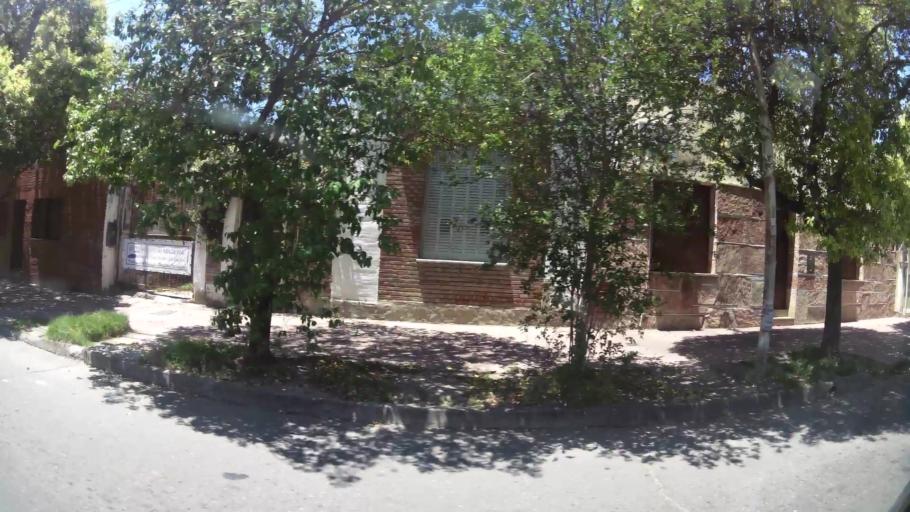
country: AR
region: Cordoba
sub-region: Departamento de Capital
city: Cordoba
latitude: -31.4078
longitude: -64.2190
